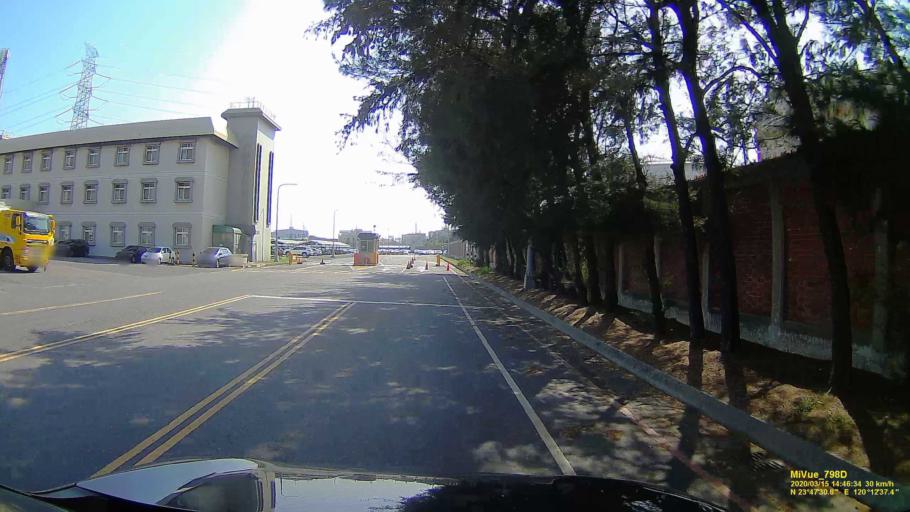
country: TW
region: Taiwan
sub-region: Yunlin
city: Douliu
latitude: 23.7918
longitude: 120.2104
